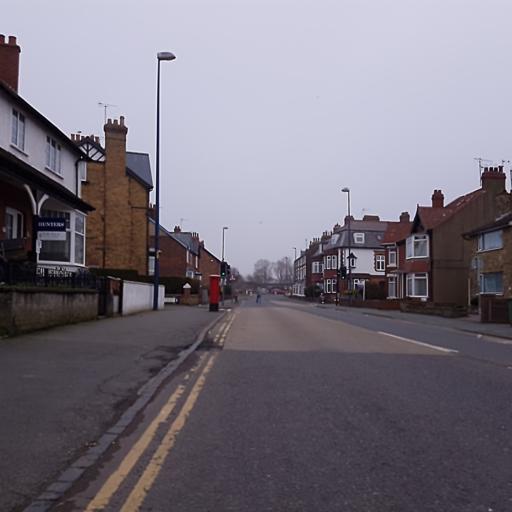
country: GB
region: England
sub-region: North Yorkshire
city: Filey
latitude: 54.2114
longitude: -0.2903
